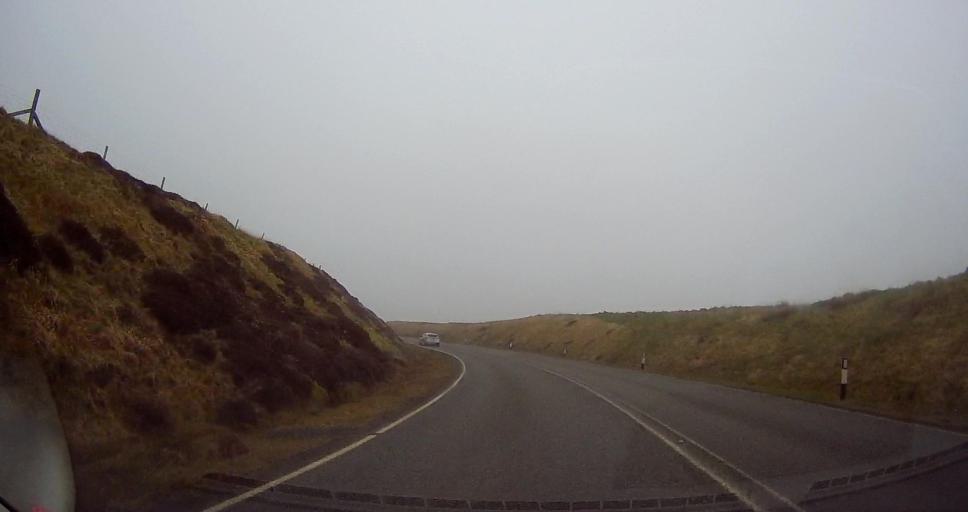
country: GB
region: Scotland
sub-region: Shetland Islands
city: Lerwick
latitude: 60.1374
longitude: -1.2314
